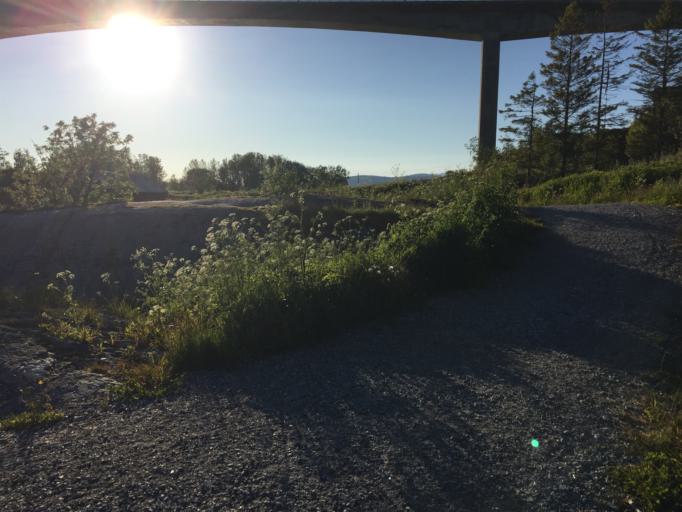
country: NO
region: Nordland
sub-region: Bodo
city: Loding
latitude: 67.2314
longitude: 14.6188
